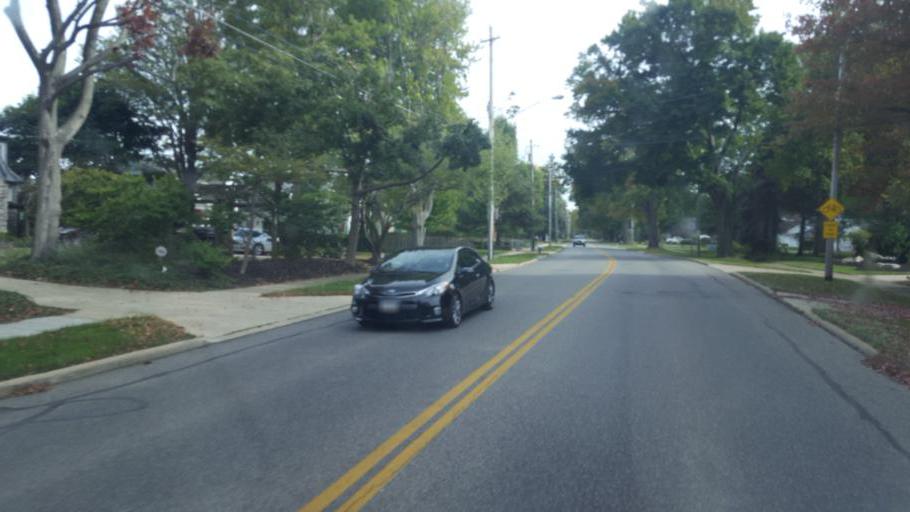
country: US
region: Ohio
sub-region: Cuyahoga County
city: Bay Village
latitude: 41.4973
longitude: -81.9583
